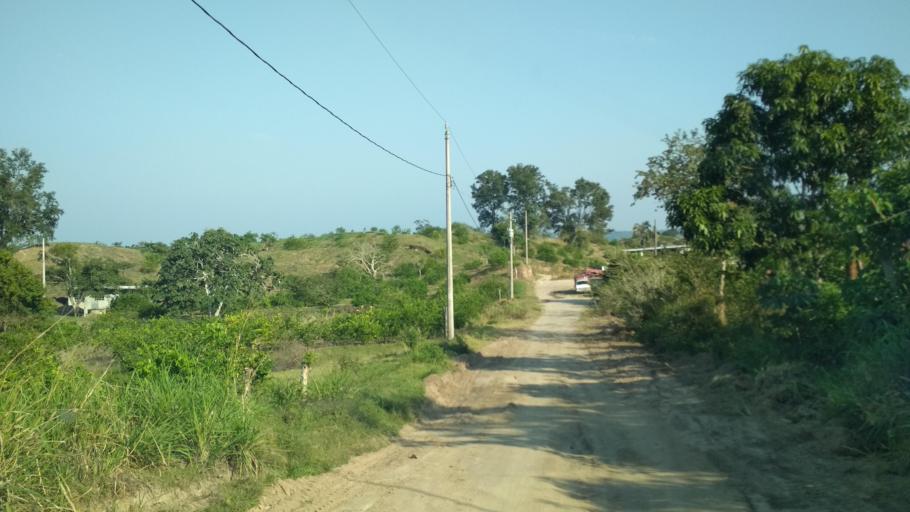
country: MX
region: Puebla
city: San Jose Acateno
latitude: 20.2195
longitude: -97.2606
